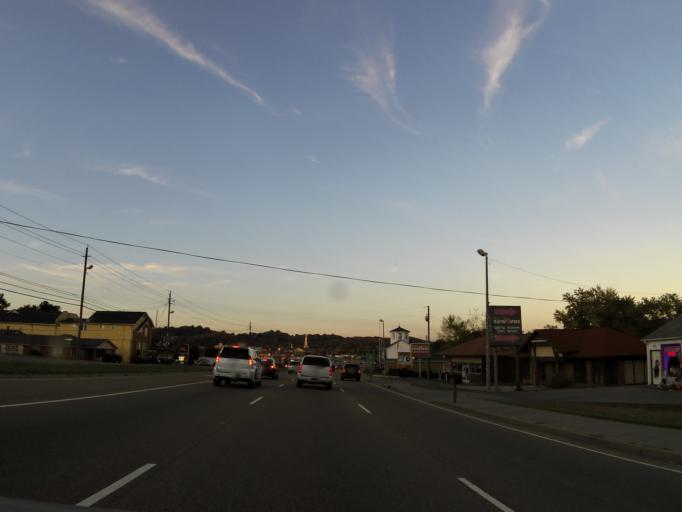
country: US
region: Tennessee
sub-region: Sevier County
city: Sevierville
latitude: 35.8571
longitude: -83.5684
